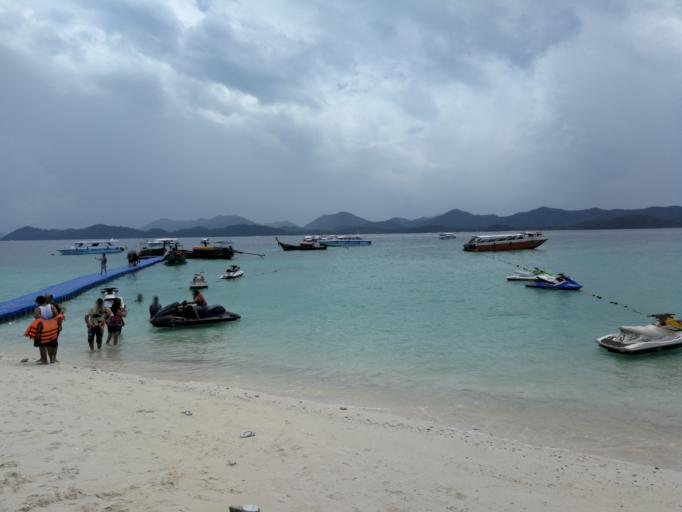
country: TH
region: Phangnga
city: Ban Phru Nai
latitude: 7.9091
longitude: 98.5500
